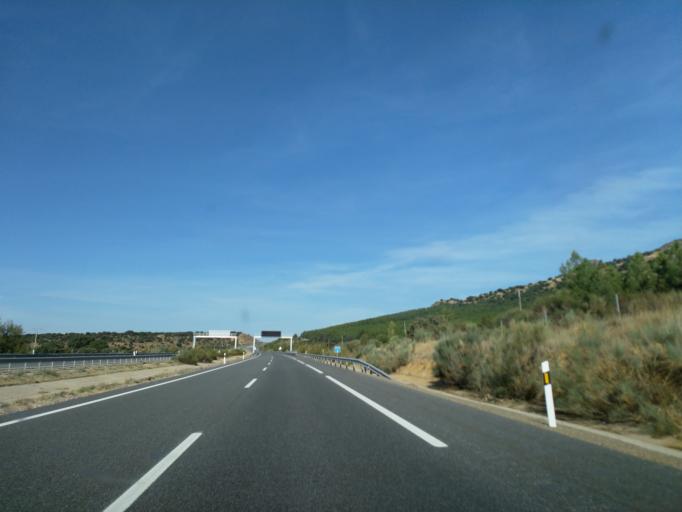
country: ES
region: Castille and Leon
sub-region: Provincia de Avila
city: Ojos-Albos
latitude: 40.7286
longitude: -4.5125
